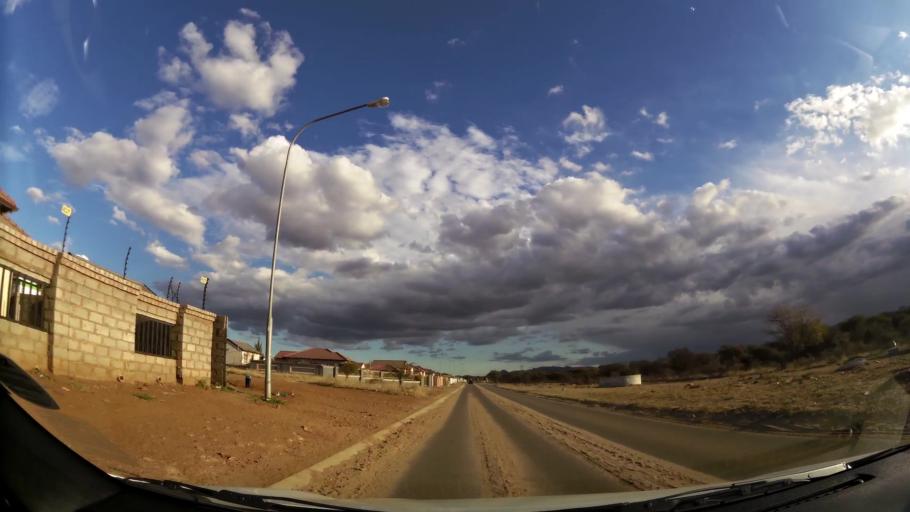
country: ZA
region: Limpopo
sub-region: Capricorn District Municipality
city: Polokwane
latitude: -23.9211
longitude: 29.4189
